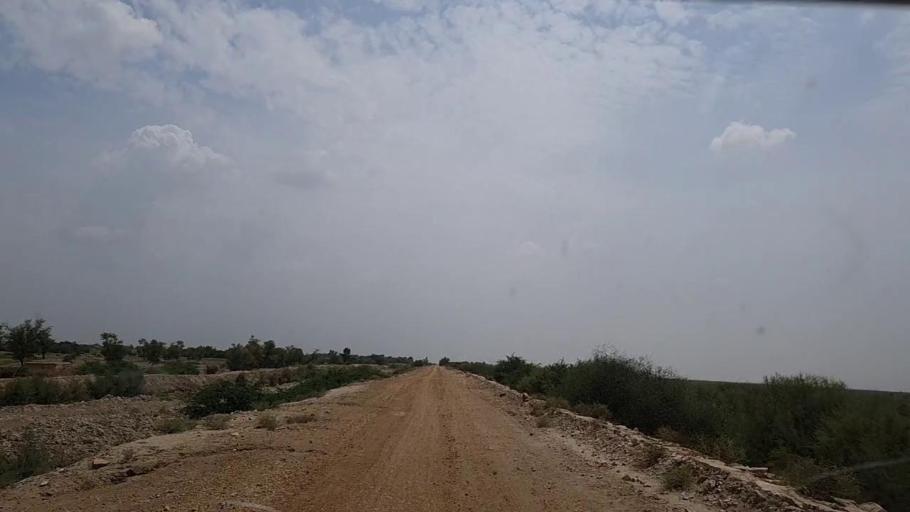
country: PK
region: Sindh
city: Phulji
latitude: 26.8154
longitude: 67.6095
